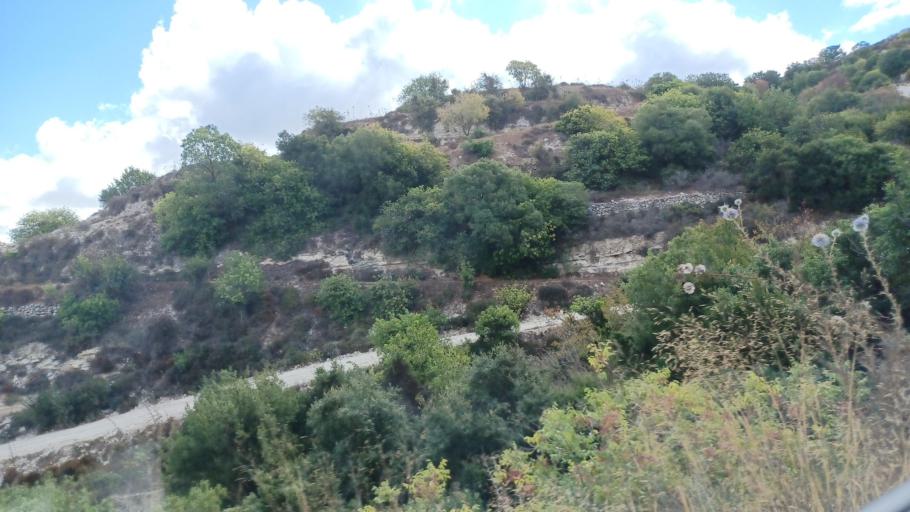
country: CY
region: Pafos
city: Tala
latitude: 34.8667
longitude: 32.4494
